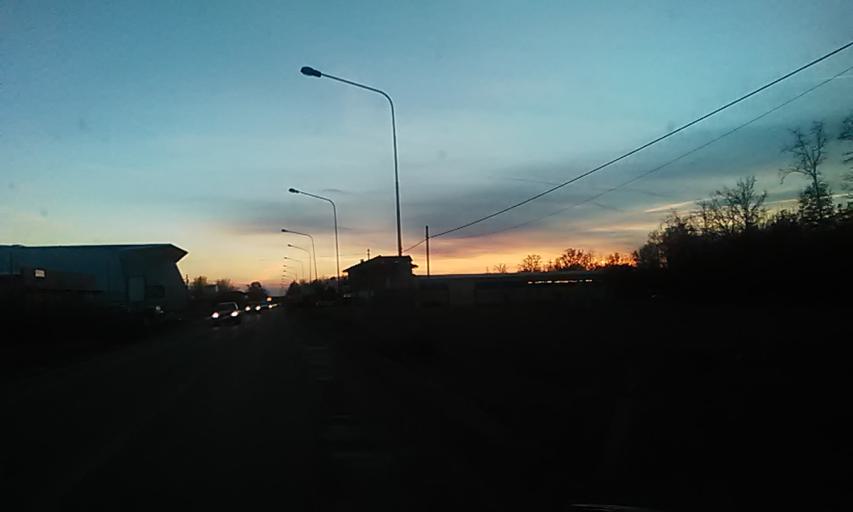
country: IT
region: Piedmont
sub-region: Provincia di Biella
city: Brusnengo
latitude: 45.5717
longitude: 8.2501
